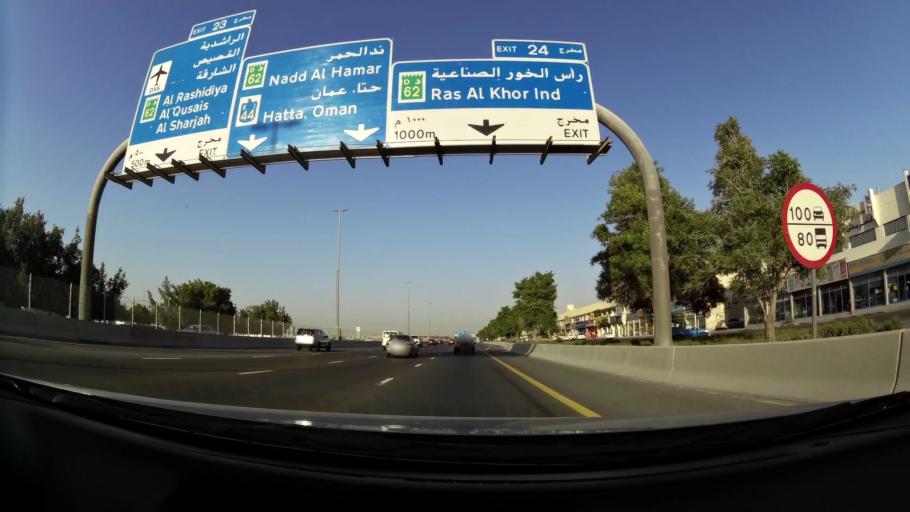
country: AE
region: Ash Shariqah
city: Sharjah
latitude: 25.1856
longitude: 55.3591
